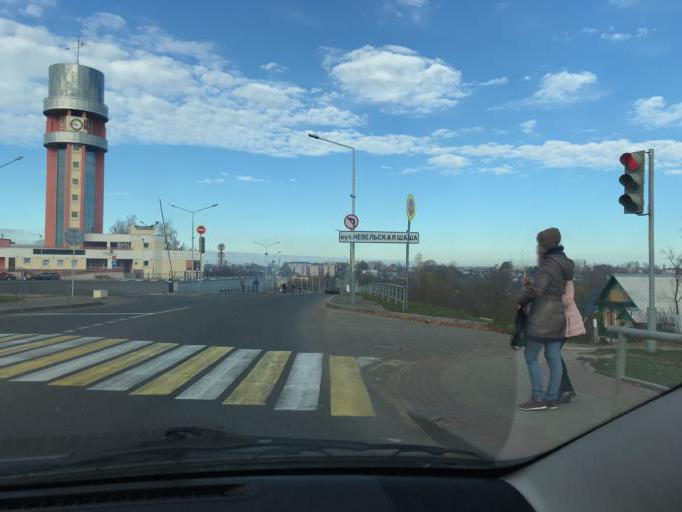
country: BY
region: Vitebsk
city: Haradok
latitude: 55.4634
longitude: 29.9831
